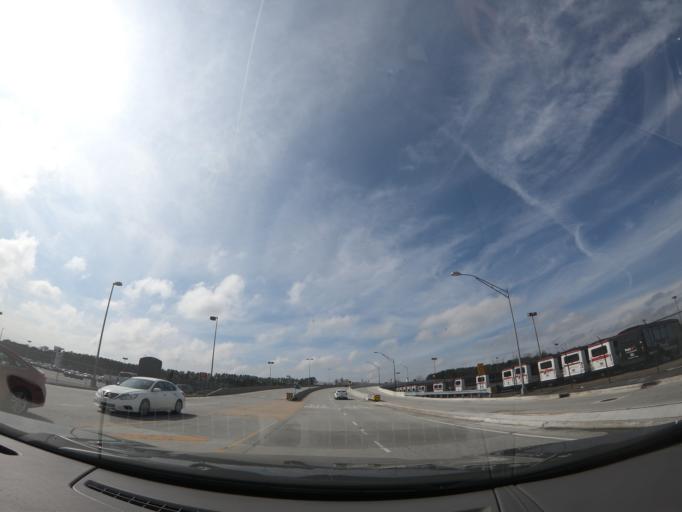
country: US
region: Georgia
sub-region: Fulton County
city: College Park
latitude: 33.6357
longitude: -84.4540
